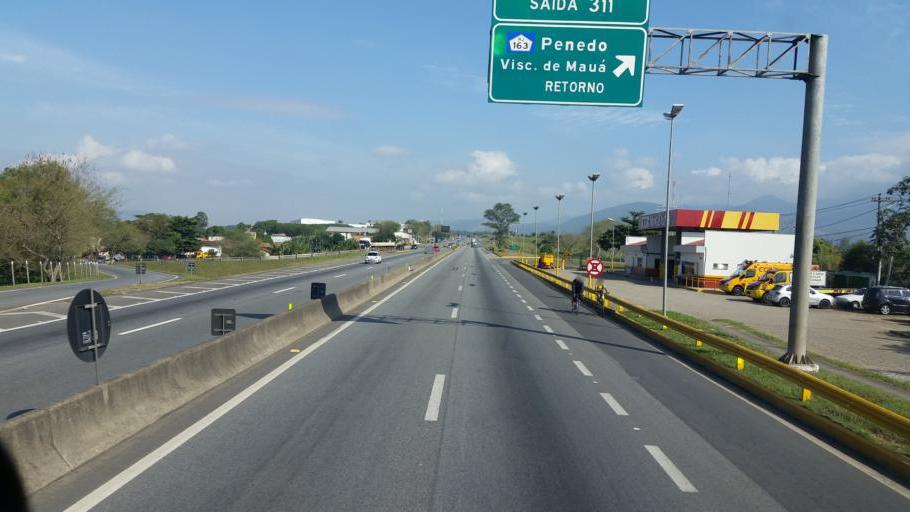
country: BR
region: Rio de Janeiro
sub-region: Resende
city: Resende
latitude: -22.4667
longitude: -44.4974
